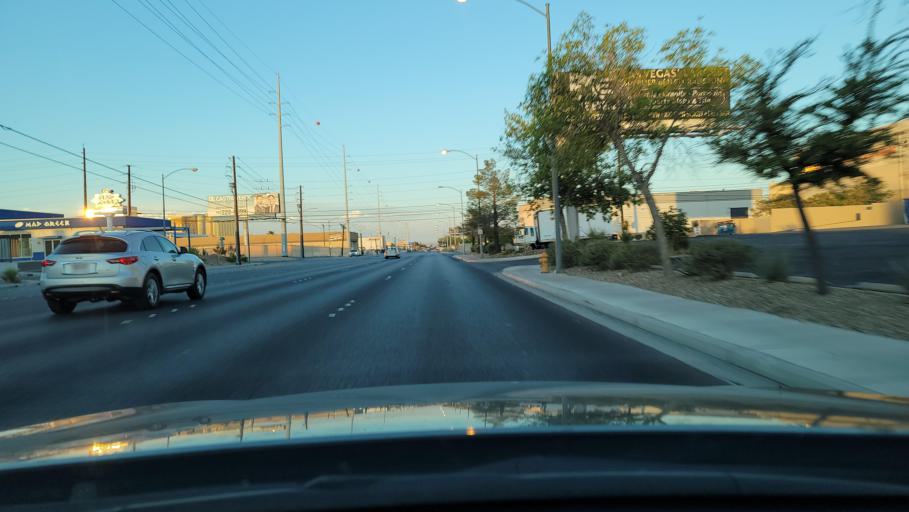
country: US
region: Nevada
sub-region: Clark County
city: Paradise
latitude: 36.0862
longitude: -115.1959
